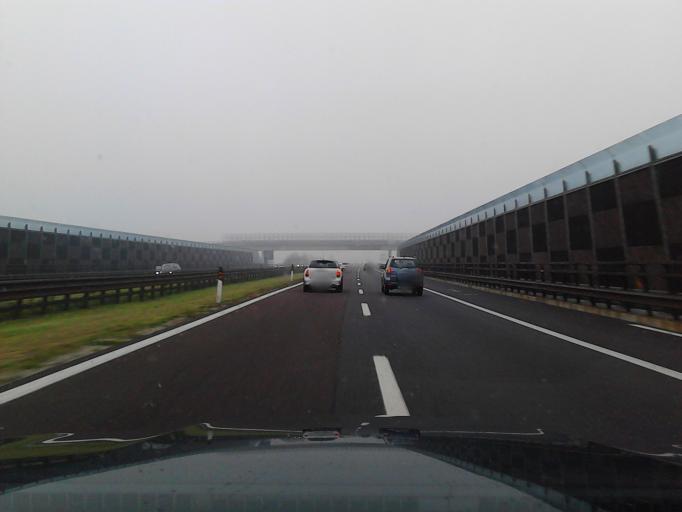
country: IT
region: Emilia-Romagna
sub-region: Provincia di Modena
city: Santa Croce Scuole
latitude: 44.7461
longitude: 10.8446
